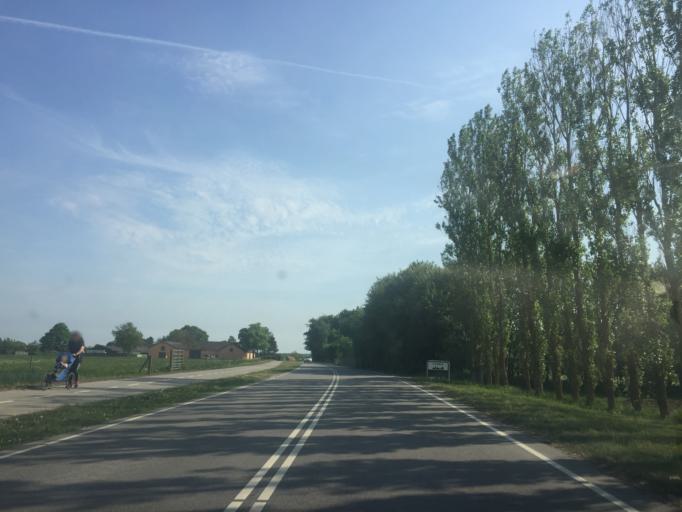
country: DK
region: Capital Region
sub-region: Egedal Kommune
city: Smorumnedre
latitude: 55.7159
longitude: 12.2963
